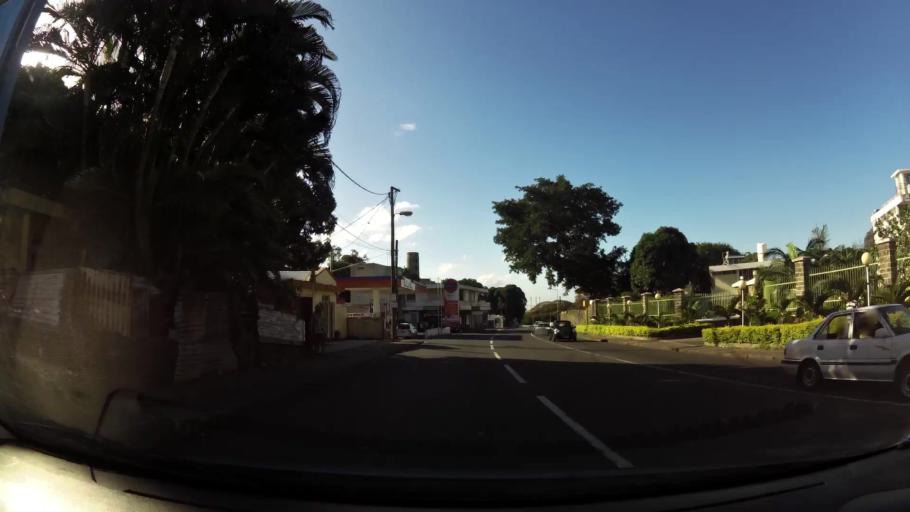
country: MU
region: Moka
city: Pailles
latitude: -20.1786
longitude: 57.4703
